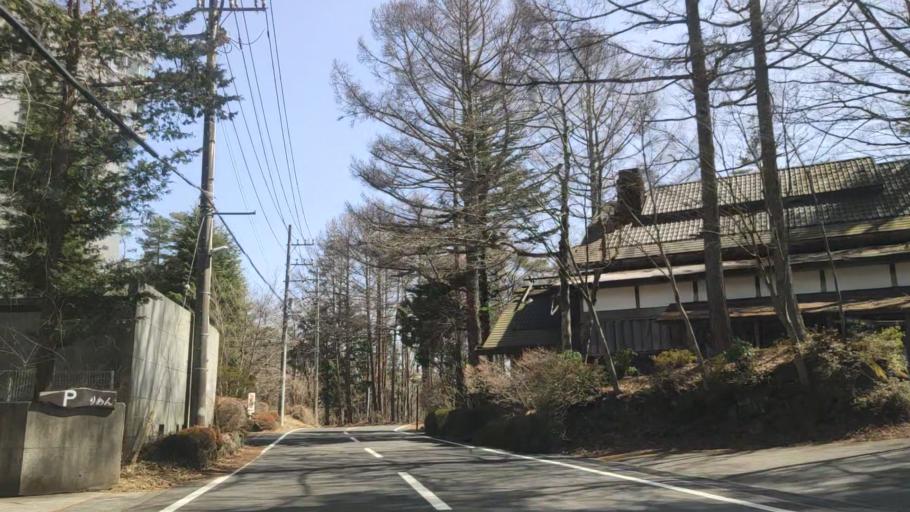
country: JP
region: Yamanashi
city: Fujikawaguchiko
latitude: 35.4585
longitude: 138.8189
